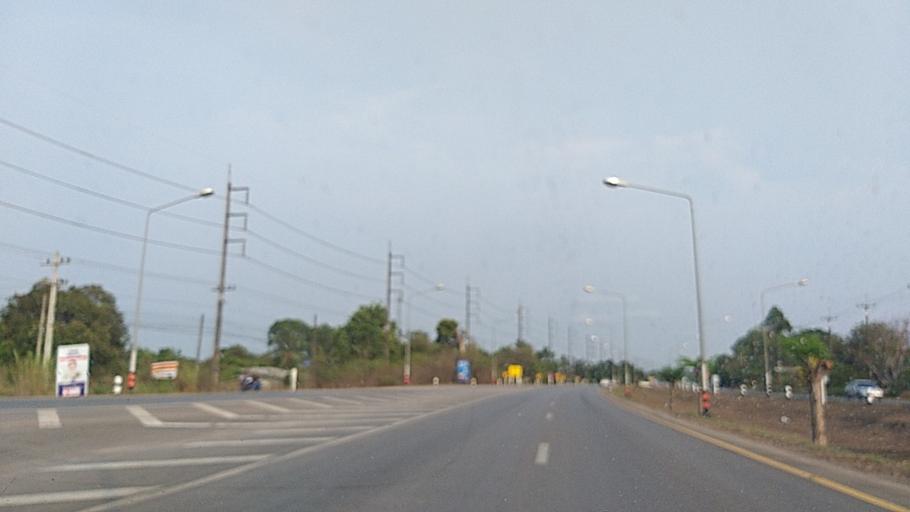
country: TH
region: Chanthaburi
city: Khlung
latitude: 12.4305
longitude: 102.3128
